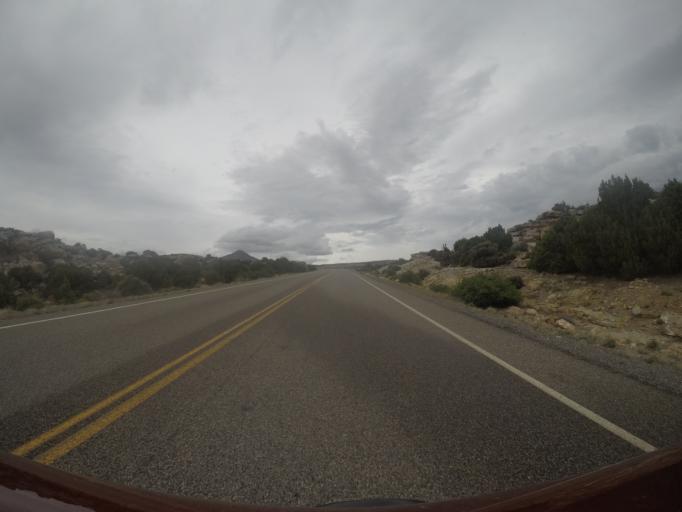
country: US
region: Wyoming
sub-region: Big Horn County
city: Lovell
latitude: 44.9944
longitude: -108.2611
